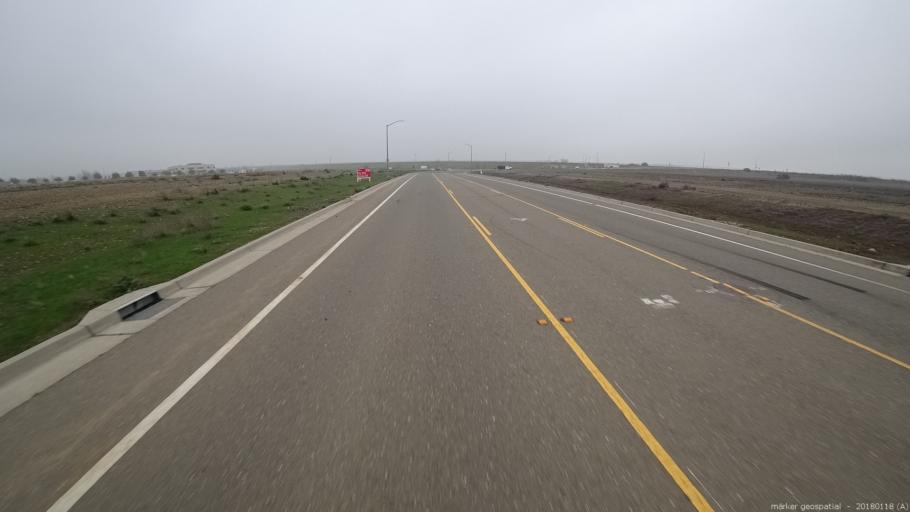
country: US
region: California
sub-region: Sacramento County
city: Rancho Cordova
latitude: 38.5699
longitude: -121.2835
